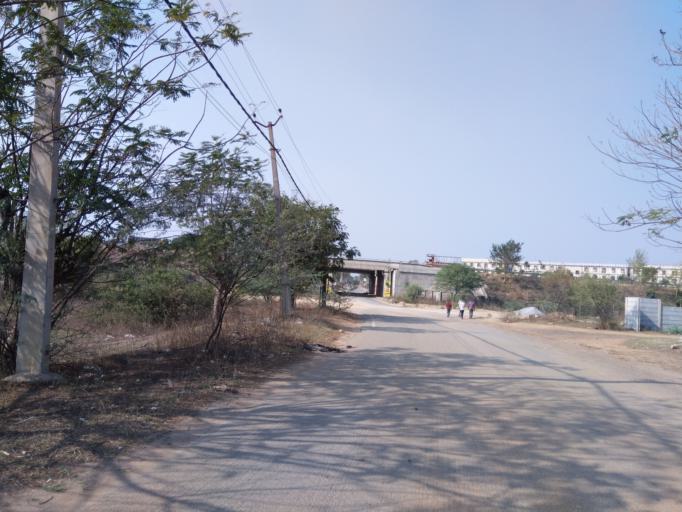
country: IN
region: Telangana
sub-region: Rangareddi
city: Quthbullapur
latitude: 17.5958
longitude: 78.4172
